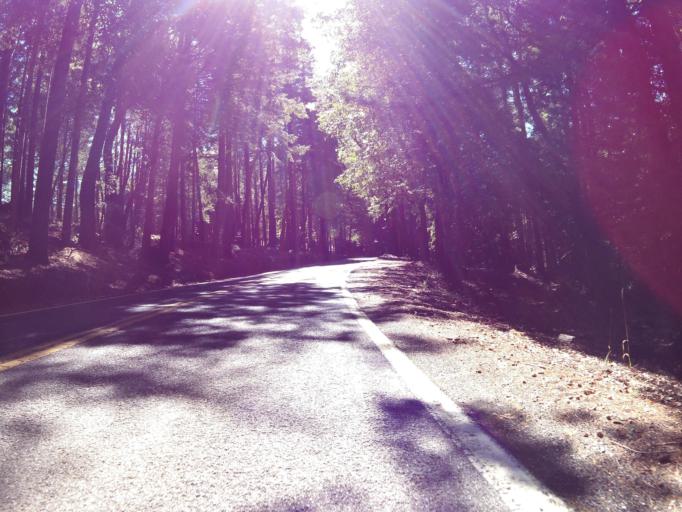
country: US
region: California
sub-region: Humboldt County
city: Redway
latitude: 39.8378
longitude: -123.7726
